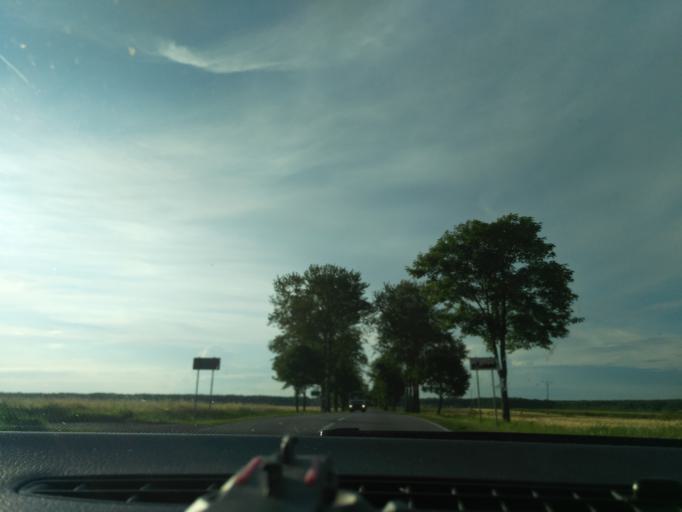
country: PL
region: Lublin Voivodeship
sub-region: Powiat krasnicki
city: Szastarka
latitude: 50.8326
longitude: 22.3060
